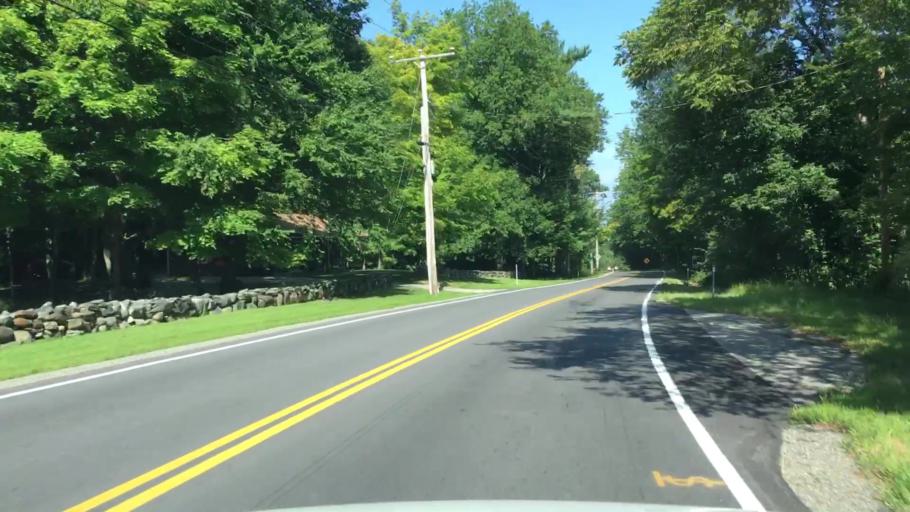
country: US
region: New Hampshire
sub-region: Rockingham County
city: Kensington
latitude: 42.9171
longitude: -70.9767
